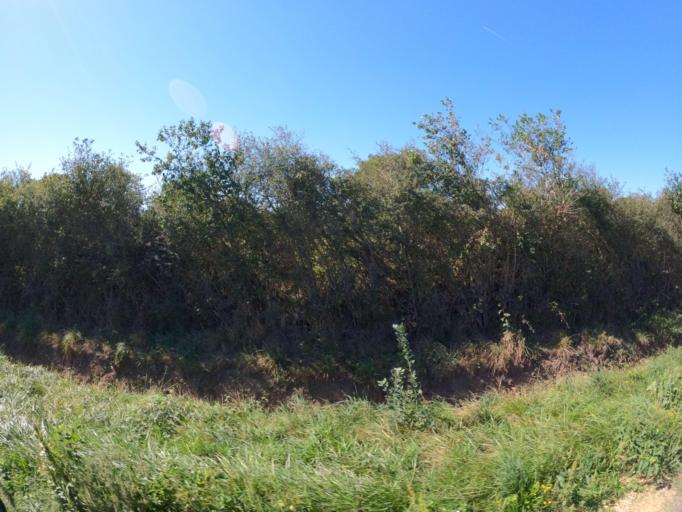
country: FR
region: Poitou-Charentes
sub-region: Departement de la Vienne
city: Saulge
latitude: 46.3888
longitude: 0.9103
